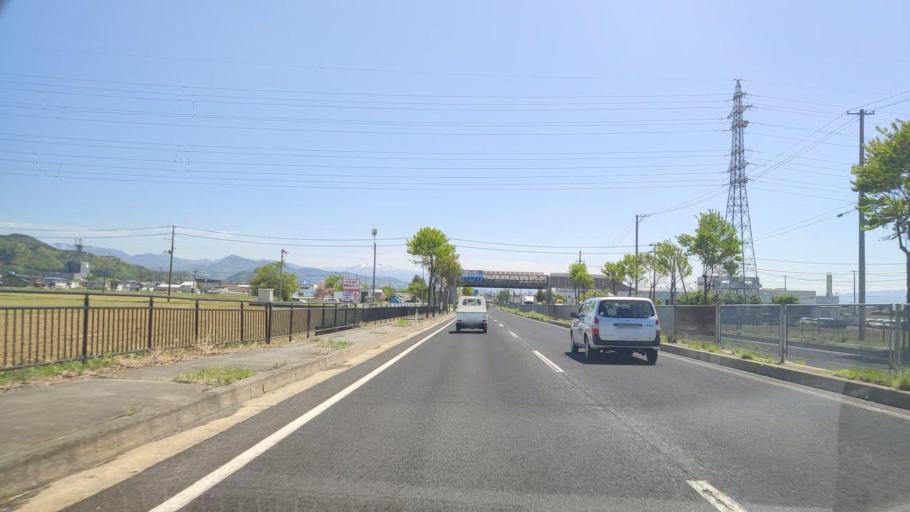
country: JP
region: Yamagata
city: Higashine
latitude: 38.4889
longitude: 140.3832
